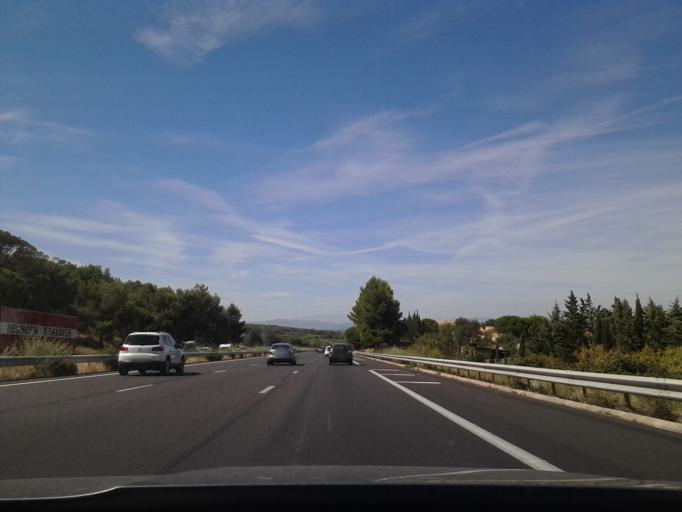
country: FR
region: Languedoc-Roussillon
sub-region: Departement de l'Aude
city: Vinassan
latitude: 43.2024
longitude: 3.0809
